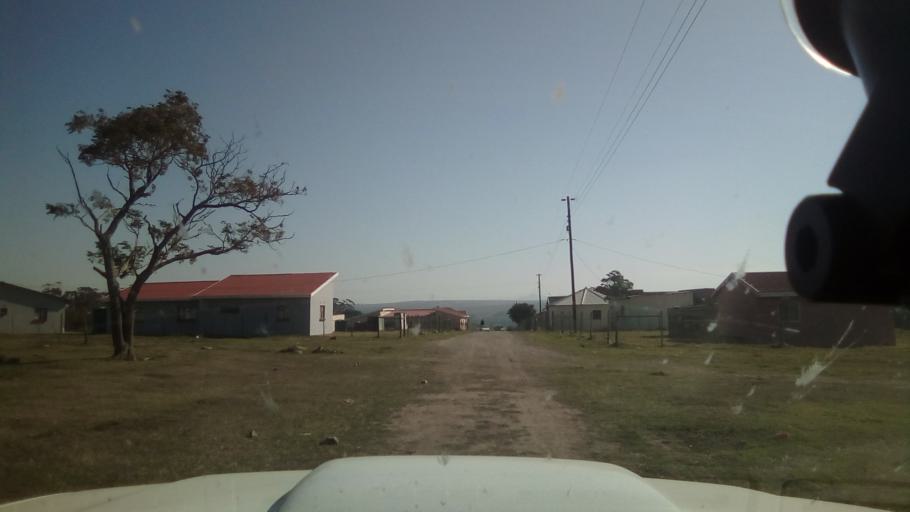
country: ZA
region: Eastern Cape
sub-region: Buffalo City Metropolitan Municipality
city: Bhisho
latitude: -32.9384
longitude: 27.3382
